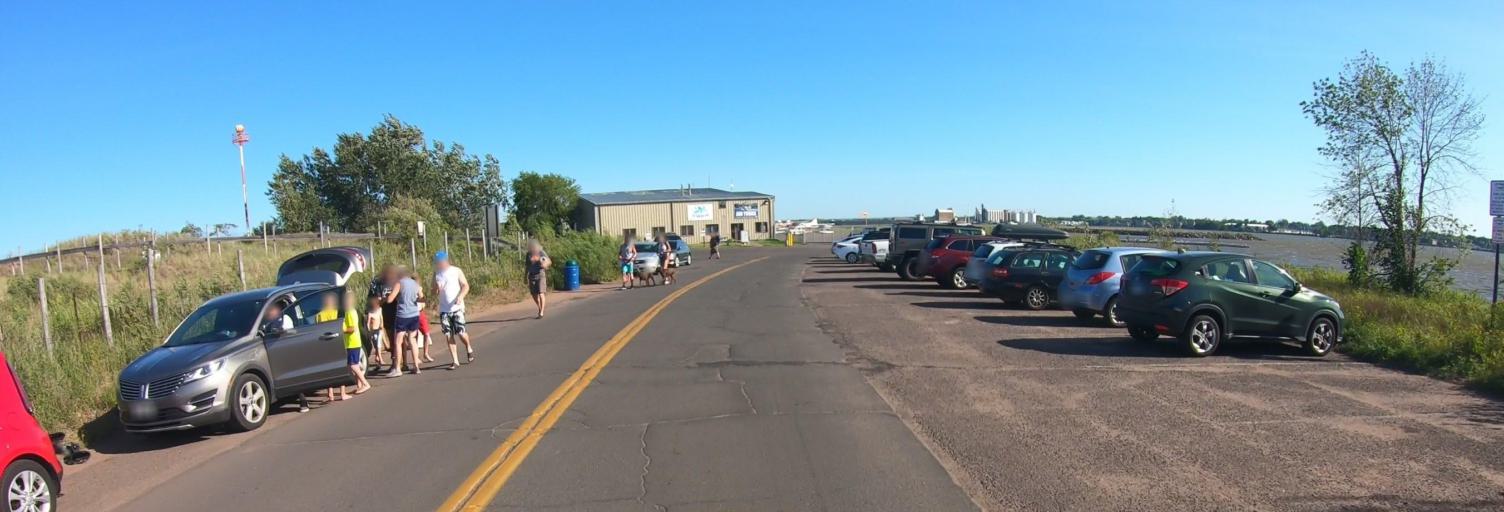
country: US
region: Wisconsin
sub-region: Douglas County
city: Superior
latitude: 46.7280
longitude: -92.0468
